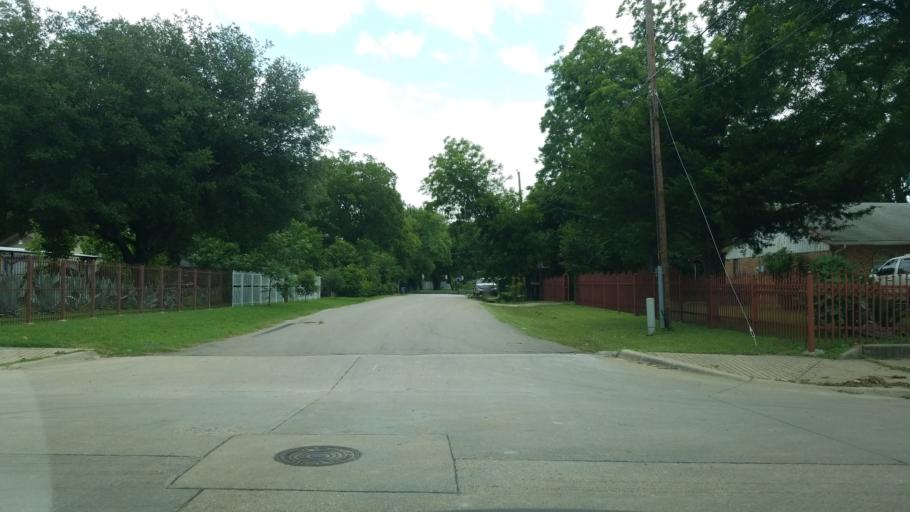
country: US
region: Texas
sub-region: Dallas County
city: Irving
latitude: 32.7917
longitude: -96.8993
